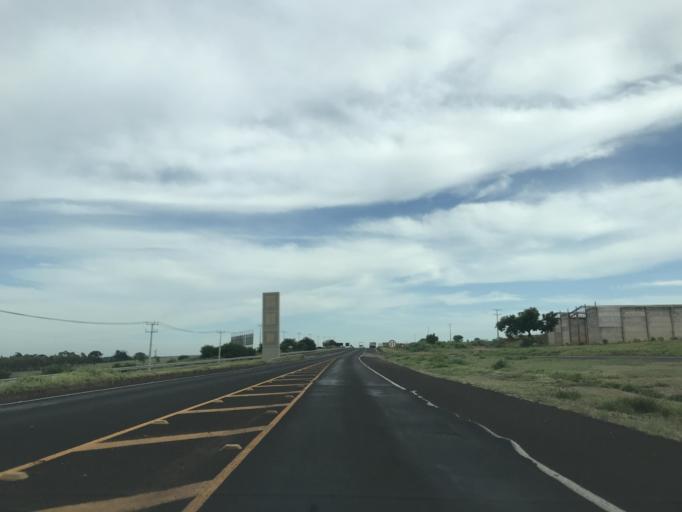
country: BR
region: Parana
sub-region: Paranavai
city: Paranavai
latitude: -23.0376
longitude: -52.4768
